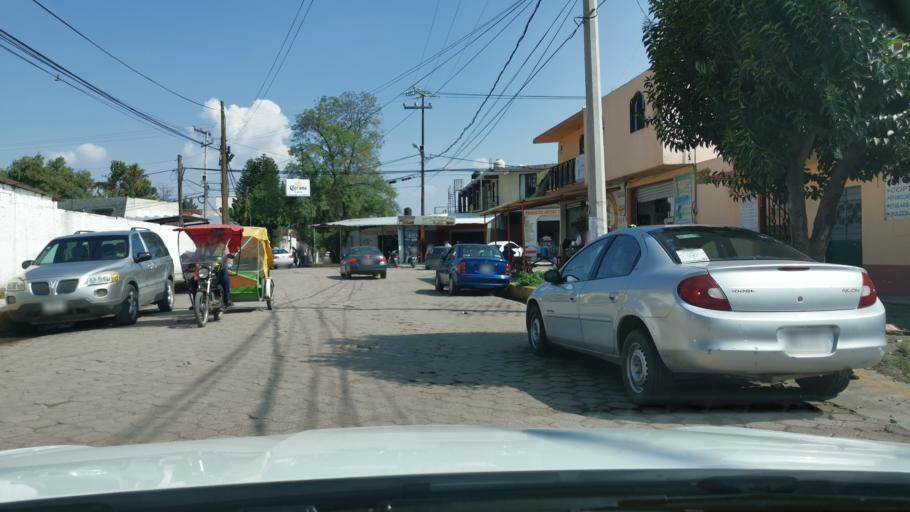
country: MX
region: Mexico
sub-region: Cuautitlan
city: San Jose del Puente
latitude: 19.7135
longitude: -99.1887
